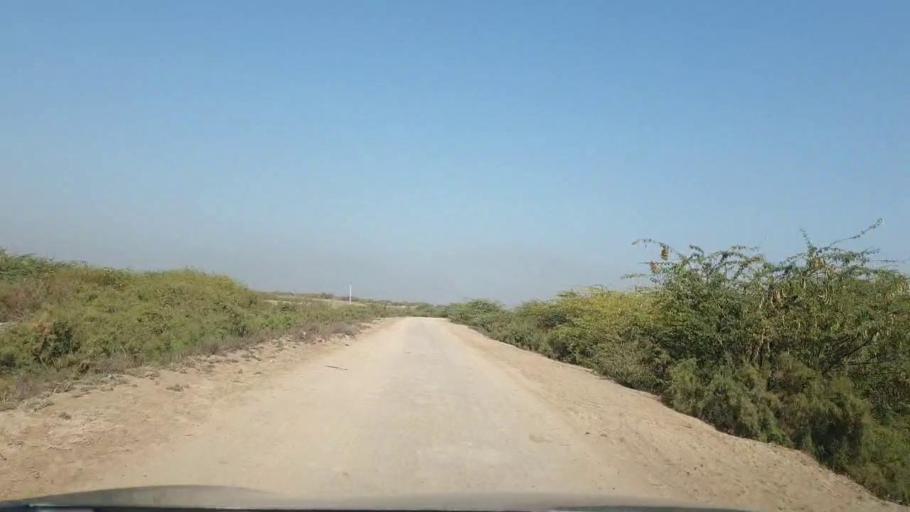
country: PK
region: Sindh
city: Berani
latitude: 25.6641
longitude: 68.9102
